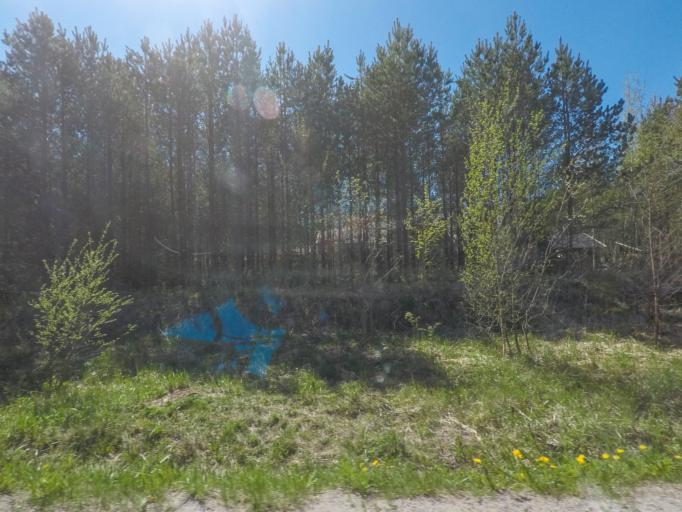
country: FI
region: Uusimaa
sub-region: Helsinki
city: Sammatti
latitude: 60.3264
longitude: 23.8138
